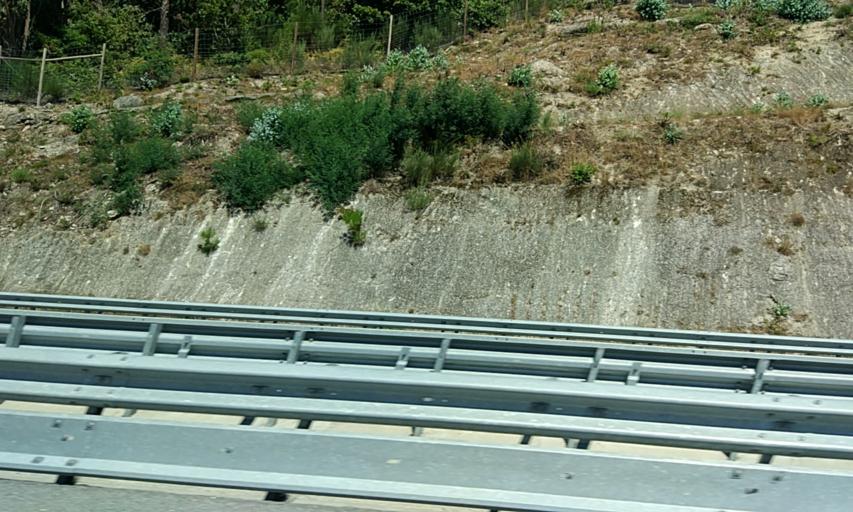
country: PT
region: Porto
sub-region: Baiao
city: Valadares
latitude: 41.2613
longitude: -7.9550
